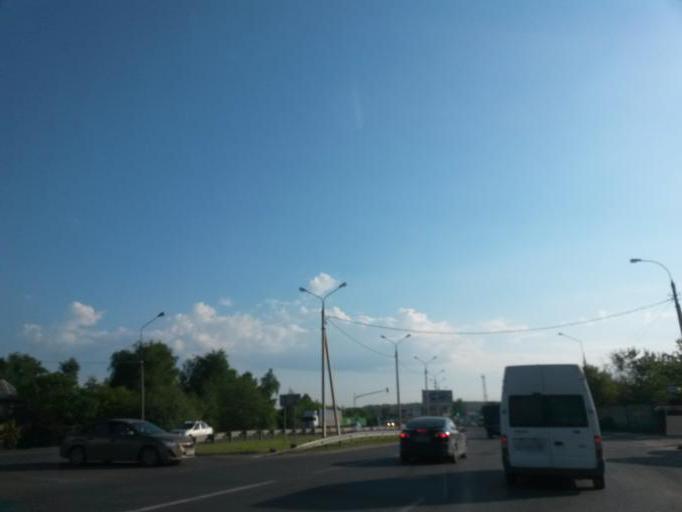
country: RU
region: Moskovskaya
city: Yam
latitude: 55.4850
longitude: 37.7472
